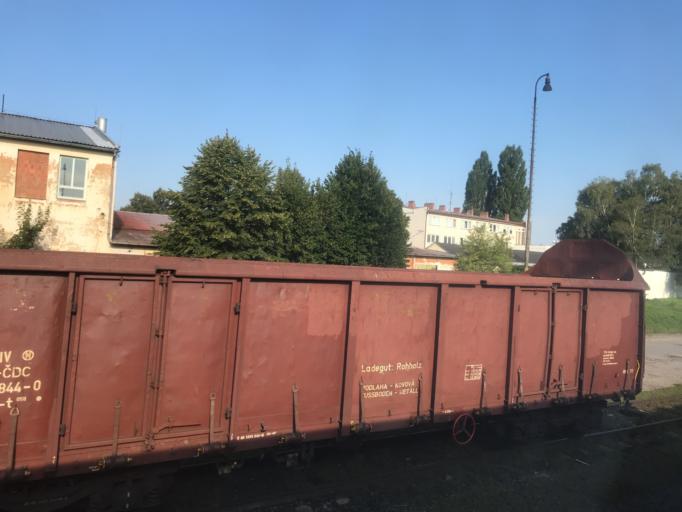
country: CZ
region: Jihocesky
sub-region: Okres Jindrichuv Hradec
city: Trebon
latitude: 49.0142
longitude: 14.7613
